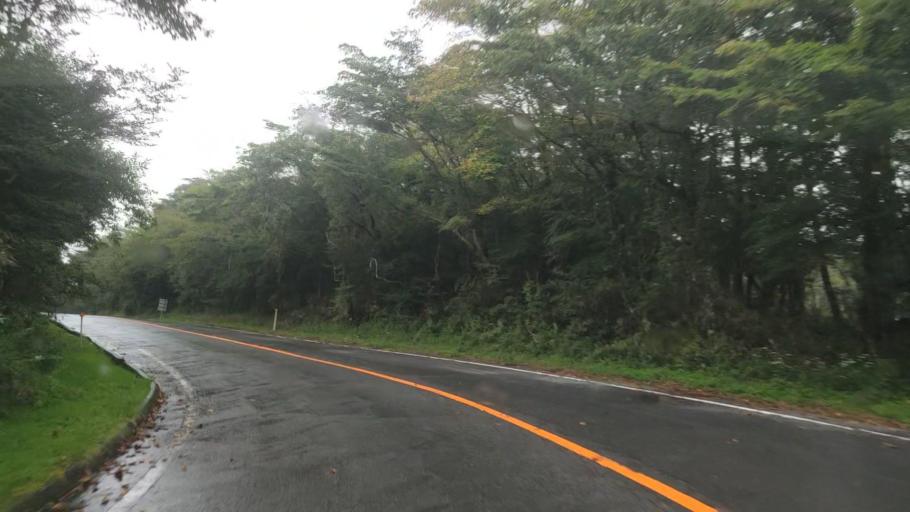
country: JP
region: Shizuoka
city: Gotemba
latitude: 35.2936
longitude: 138.7764
